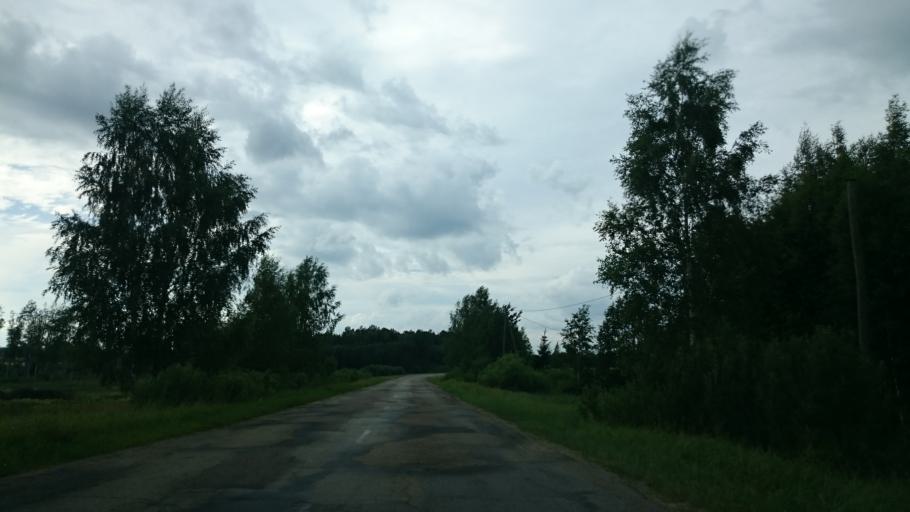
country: LV
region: Seja
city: Loja
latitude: 57.2186
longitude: 24.5703
